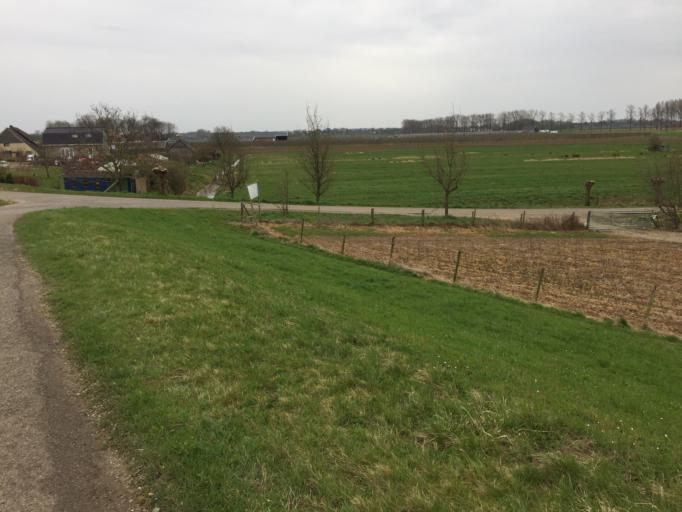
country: NL
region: Utrecht
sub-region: Gemeente Utrechtse Heuvelrug
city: Amerongen
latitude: 51.9804
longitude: 5.4694
